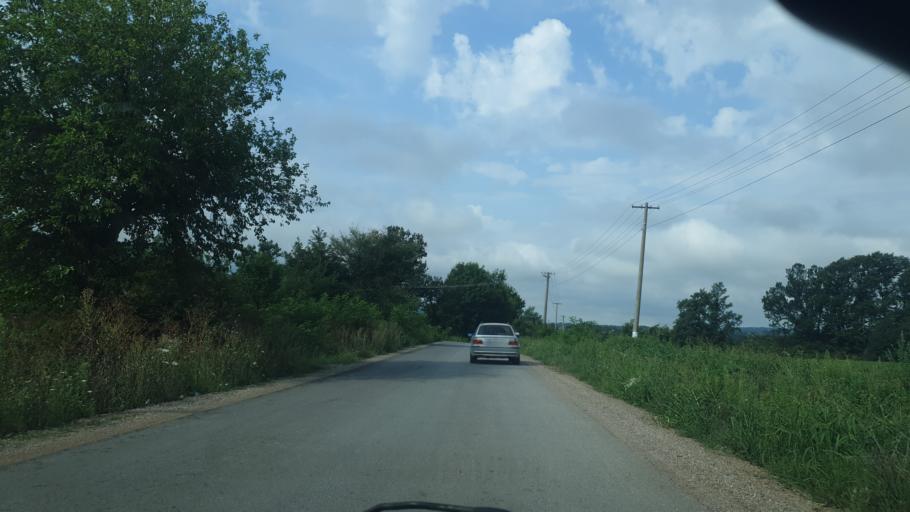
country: RS
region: Central Serbia
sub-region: Sumadijski Okrug
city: Kragujevac
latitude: 44.1133
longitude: 20.8378
